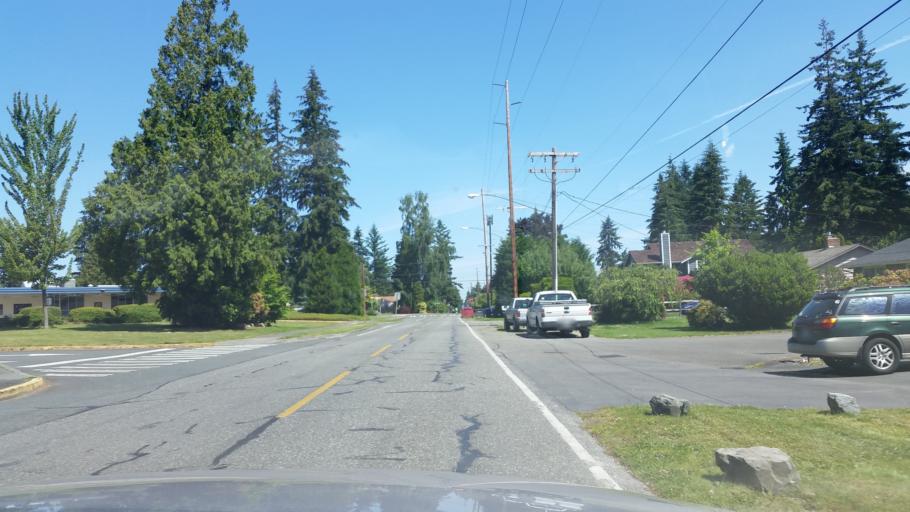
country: US
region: Washington
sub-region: Snohomish County
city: Esperance
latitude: 47.7982
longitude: -122.3616
